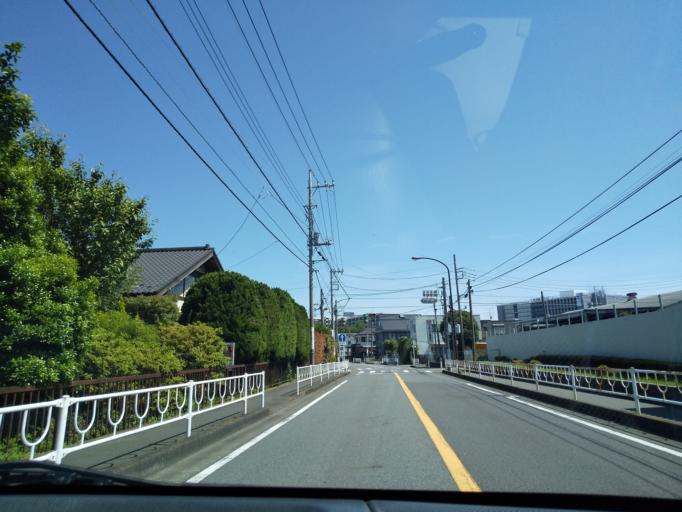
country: JP
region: Kanagawa
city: Zama
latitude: 35.5660
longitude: 139.3561
